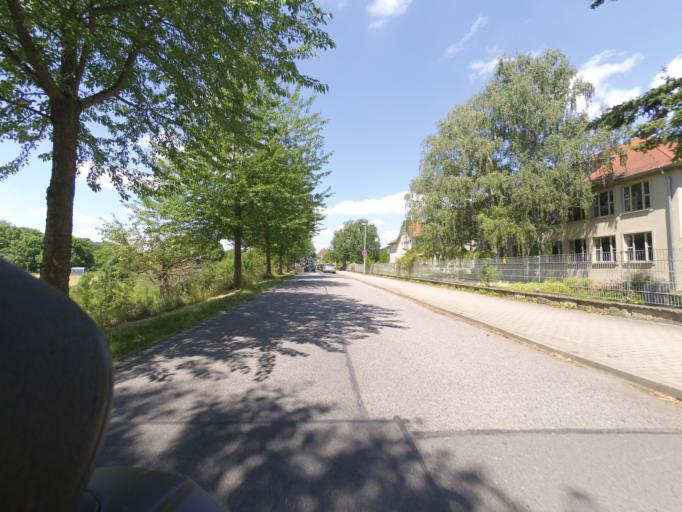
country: DE
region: Saxony
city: Heidenau
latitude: 51.0050
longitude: 13.8763
